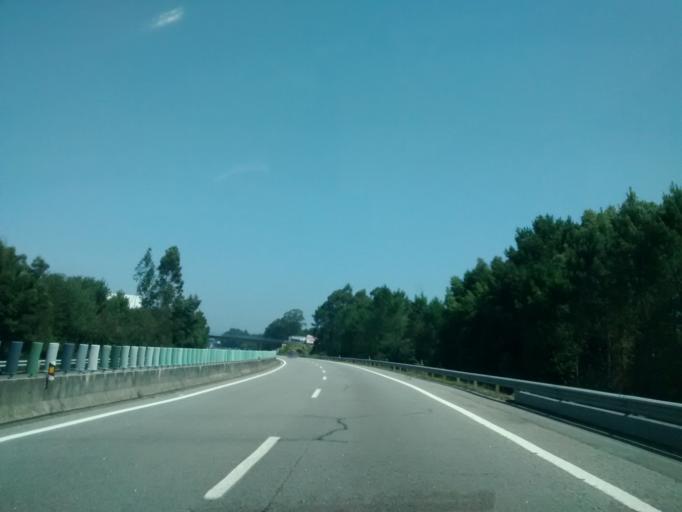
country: PT
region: Viana do Castelo
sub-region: Viana do Castelo
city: Darque
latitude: 41.6313
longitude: -8.7604
